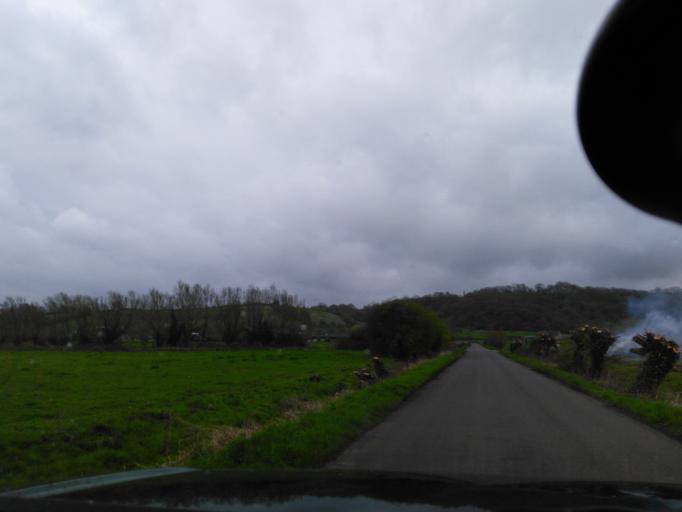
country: GB
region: England
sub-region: Somerset
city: Langport
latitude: 51.0915
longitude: -2.8203
